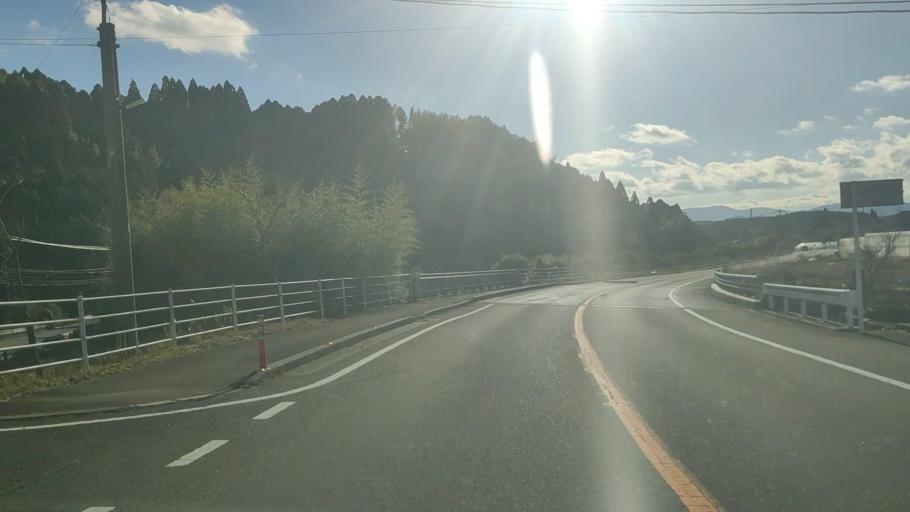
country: JP
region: Fukuoka
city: Maebaru-chuo
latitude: 33.4503
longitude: 130.2755
